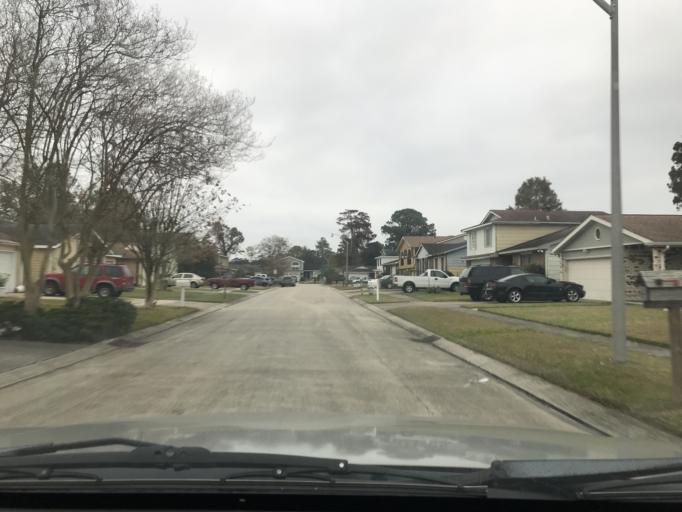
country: US
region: Louisiana
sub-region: Jefferson Parish
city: Woodmere
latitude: 29.8652
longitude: -90.0780
